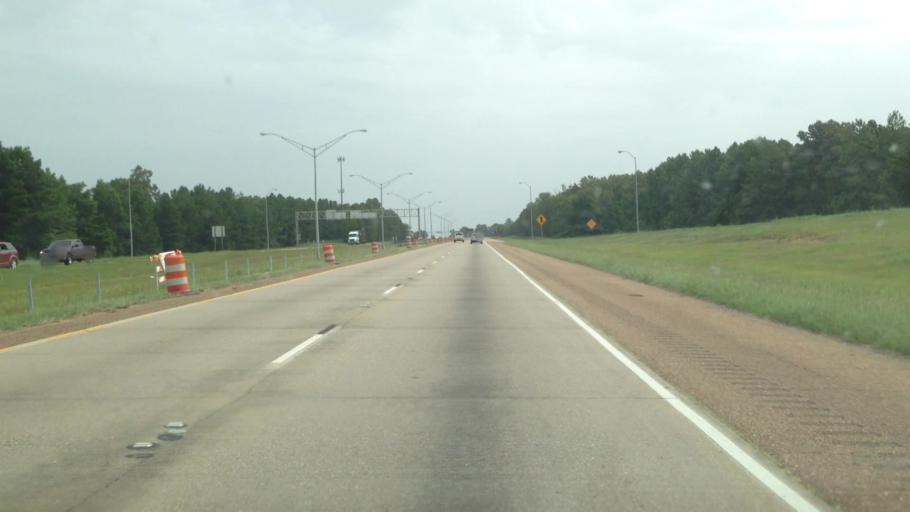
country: US
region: Louisiana
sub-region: Caddo Parish
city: Shreveport
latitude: 32.4864
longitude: -93.8275
